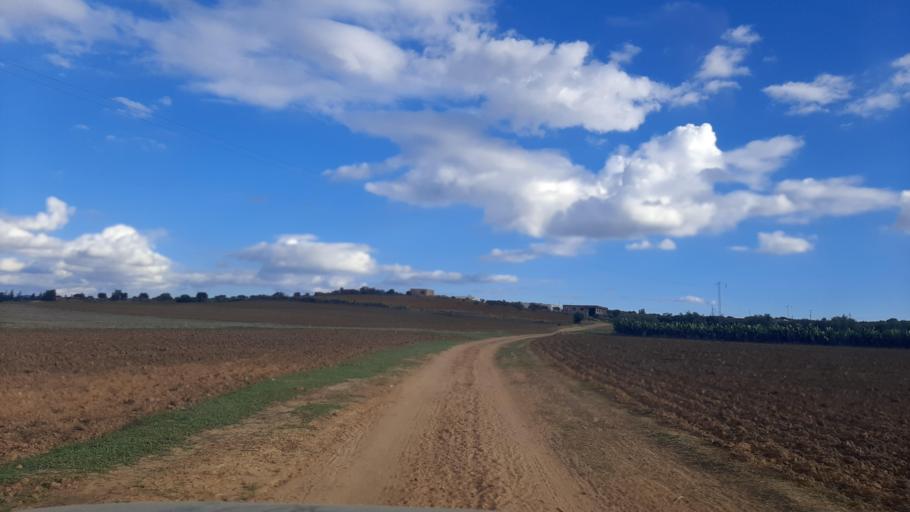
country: TN
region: Nabul
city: Bu `Urqub
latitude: 36.4452
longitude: 10.5034
